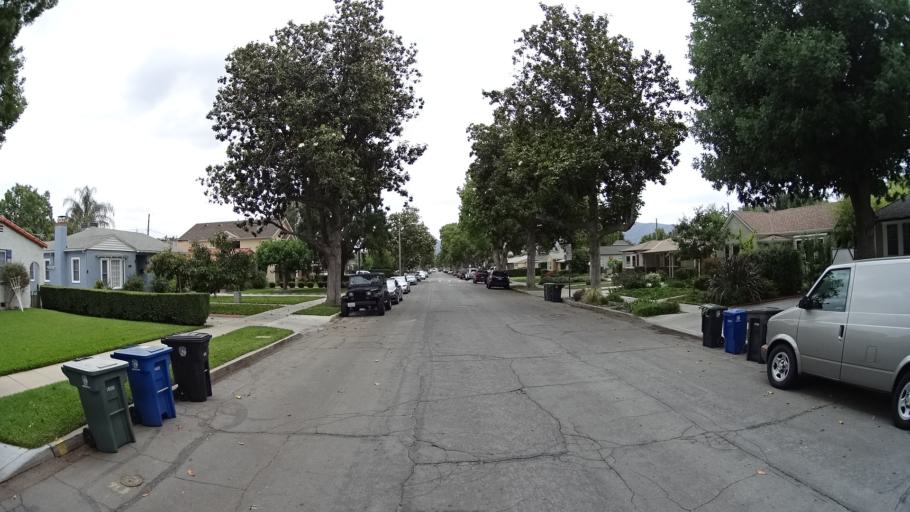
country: US
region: California
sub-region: Los Angeles County
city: Burbank
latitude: 34.1746
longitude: -118.3229
